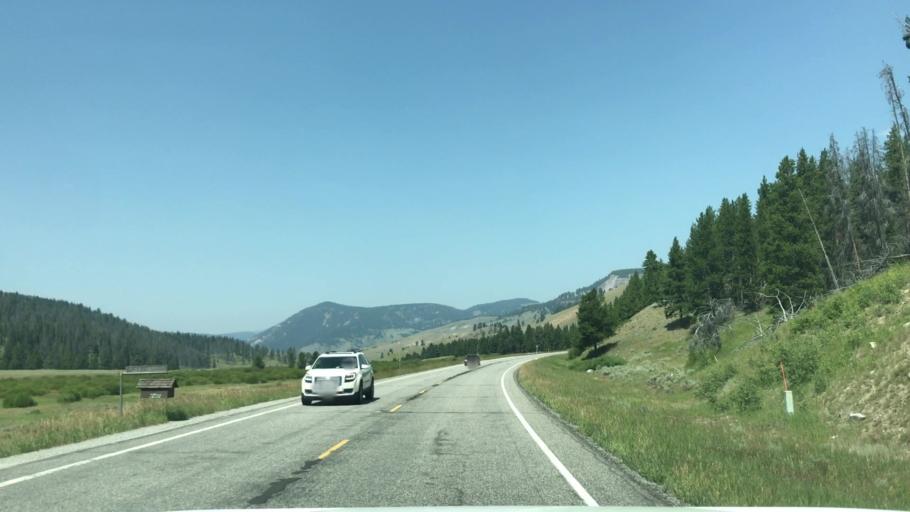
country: US
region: Montana
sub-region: Gallatin County
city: Big Sky
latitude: 45.0297
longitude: -111.1094
